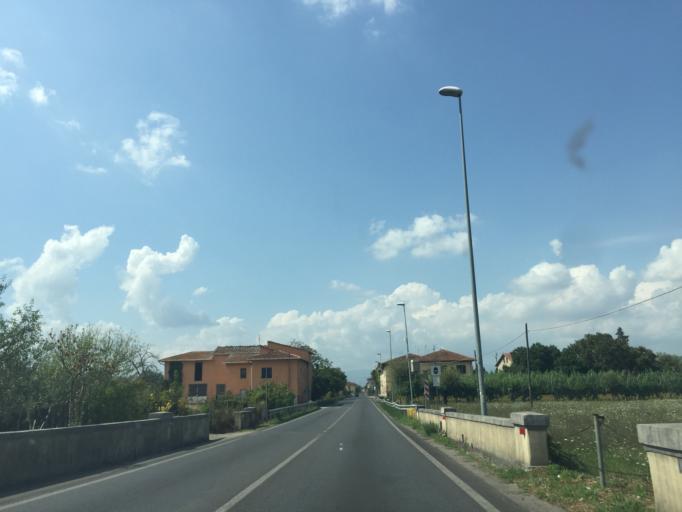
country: IT
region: Tuscany
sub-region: Provincia di Prato
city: Seano
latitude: 43.8379
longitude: 11.0239
